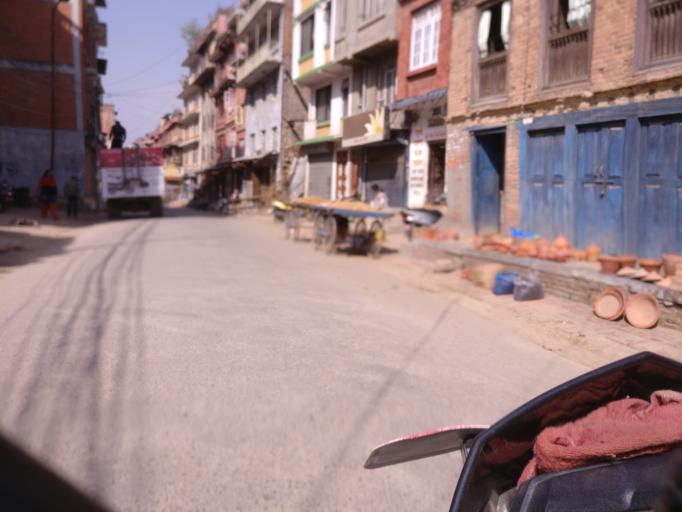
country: NP
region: Central Region
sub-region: Bagmati Zone
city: Patan
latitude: 27.6703
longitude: 85.3257
